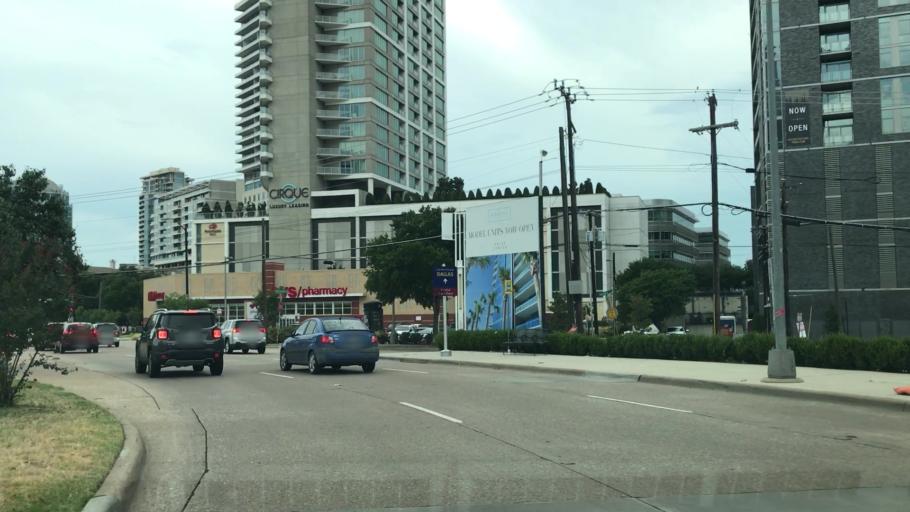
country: US
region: Texas
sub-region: Dallas County
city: Dallas
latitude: 32.7913
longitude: -96.8077
